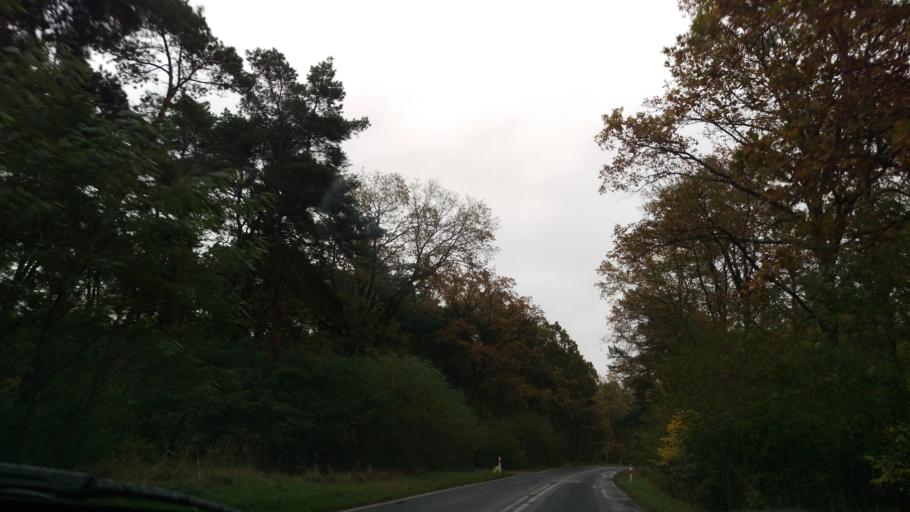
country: PL
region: West Pomeranian Voivodeship
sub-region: Szczecin
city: Szczecin
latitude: 53.3970
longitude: 14.6932
